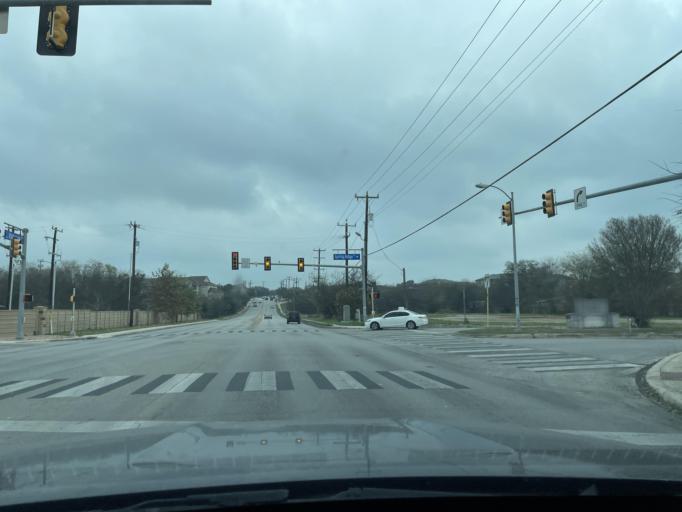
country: US
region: Texas
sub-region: Bexar County
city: Leon Valley
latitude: 29.5572
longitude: -98.6205
